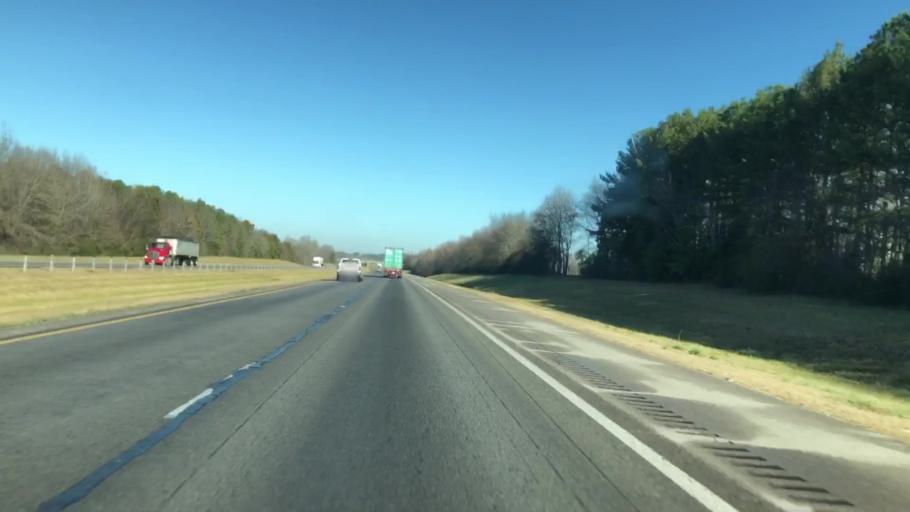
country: US
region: Alabama
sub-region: Limestone County
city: Athens
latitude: 34.8023
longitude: -86.9386
